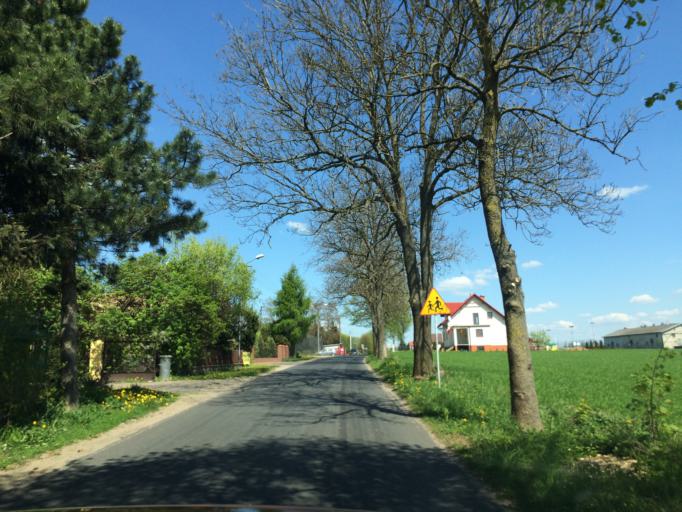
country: PL
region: Warmian-Masurian Voivodeship
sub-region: Powiat ilawski
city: Lubawa
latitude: 53.4085
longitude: 19.7522
